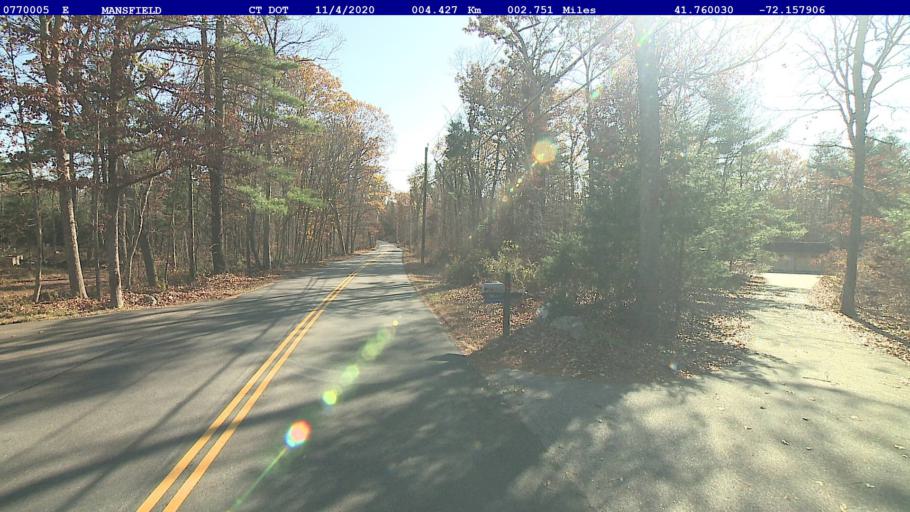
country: US
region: Connecticut
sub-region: Windham County
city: Windham
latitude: 41.7600
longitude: -72.1579
